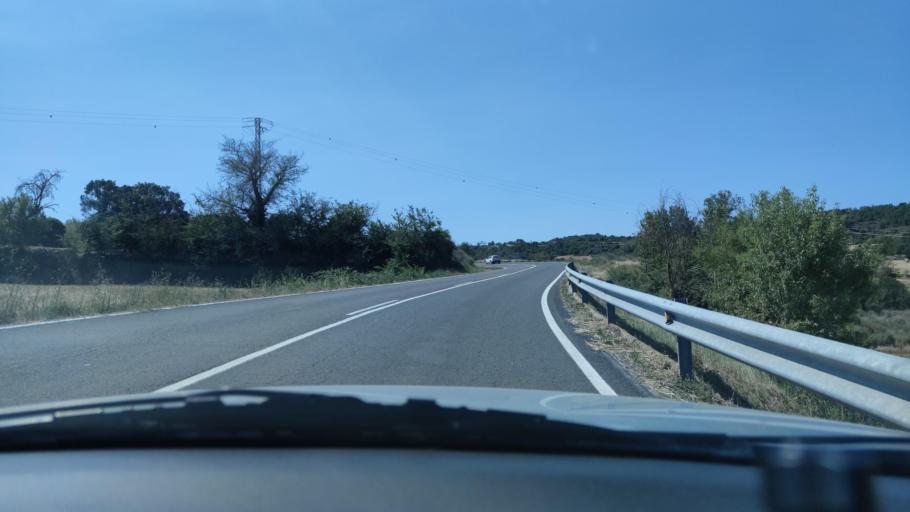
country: ES
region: Catalonia
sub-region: Provincia de Lleida
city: Cervera
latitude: 41.6203
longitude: 1.3387
